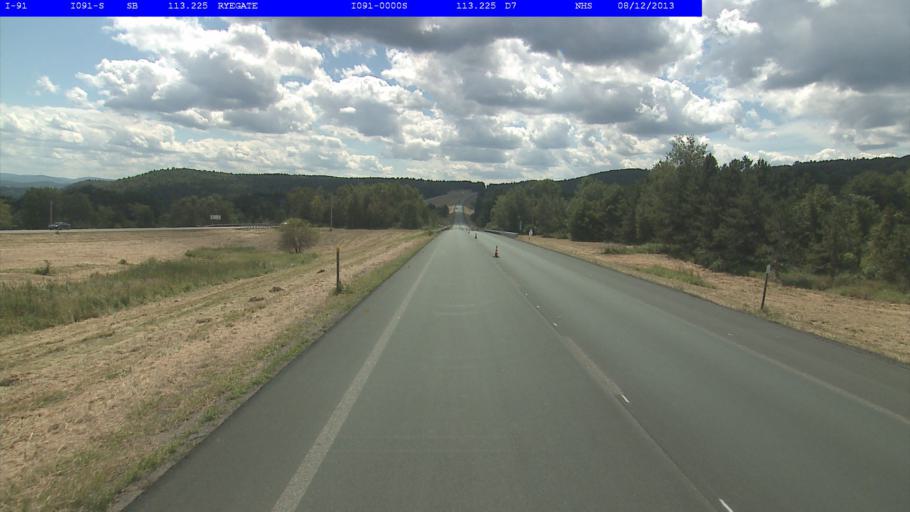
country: US
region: New Hampshire
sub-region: Grafton County
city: Woodsville
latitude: 44.1998
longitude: -72.0714
